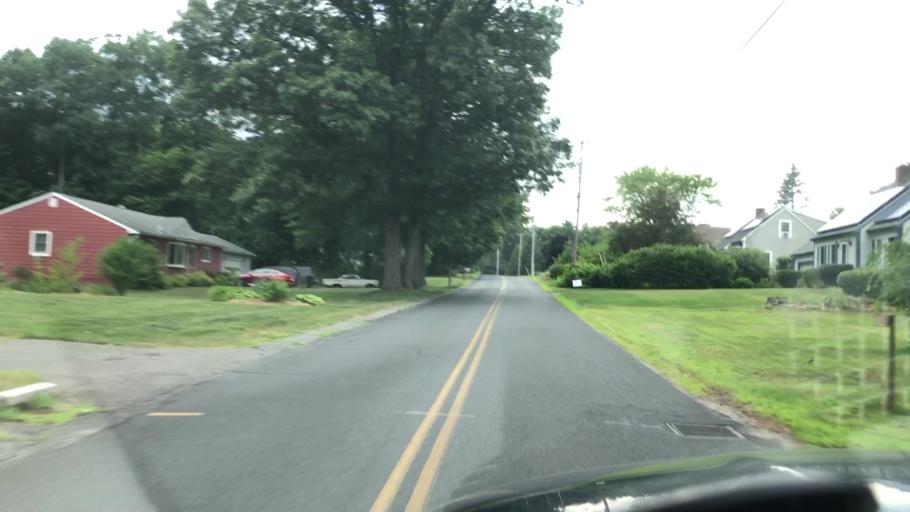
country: US
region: Massachusetts
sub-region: Hampshire County
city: Easthampton
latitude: 42.2398
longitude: -72.6721
